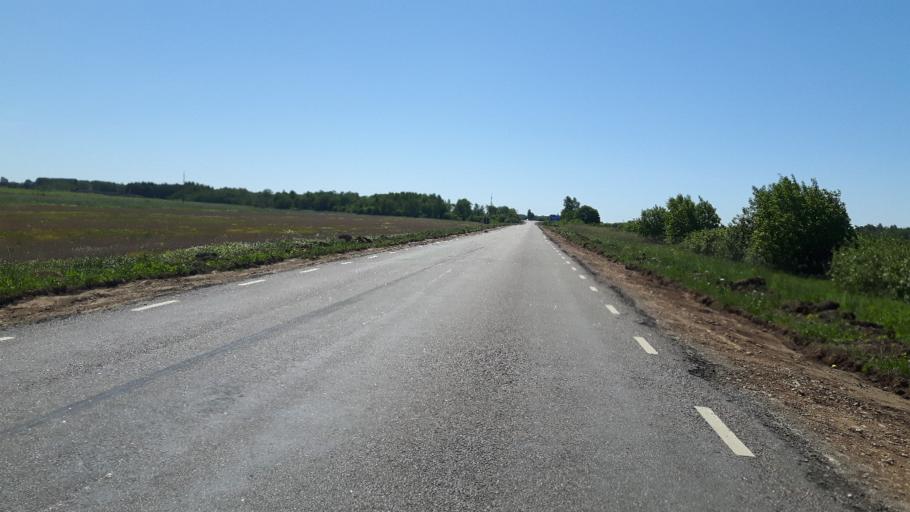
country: EE
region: Ida-Virumaa
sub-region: Narva-Joesuu linn
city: Narva-Joesuu
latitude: 59.3847
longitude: 27.9207
